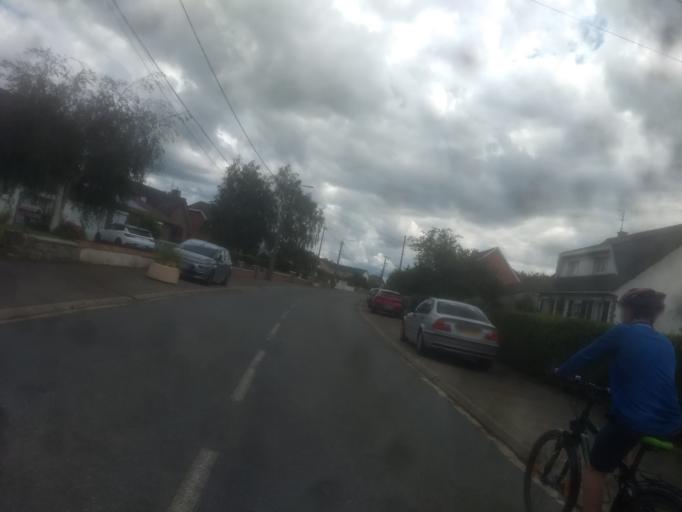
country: FR
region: Nord-Pas-de-Calais
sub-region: Departement du Pas-de-Calais
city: Agny
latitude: 50.2267
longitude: 2.7421
